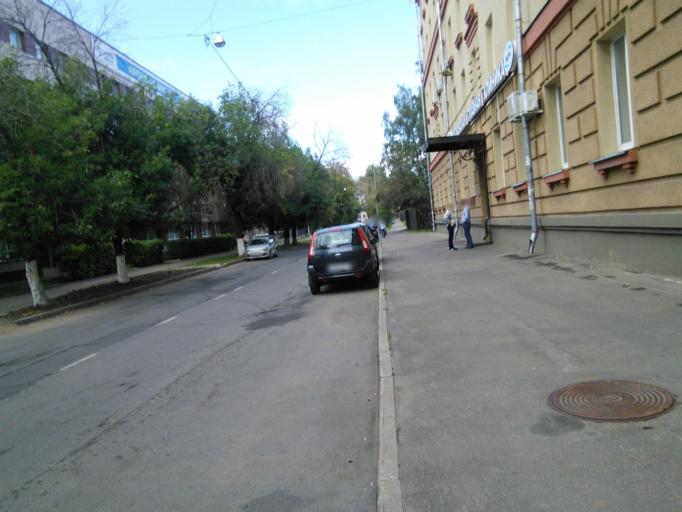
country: RU
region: Moscow
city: Lefortovo
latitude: 55.7829
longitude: 37.7147
